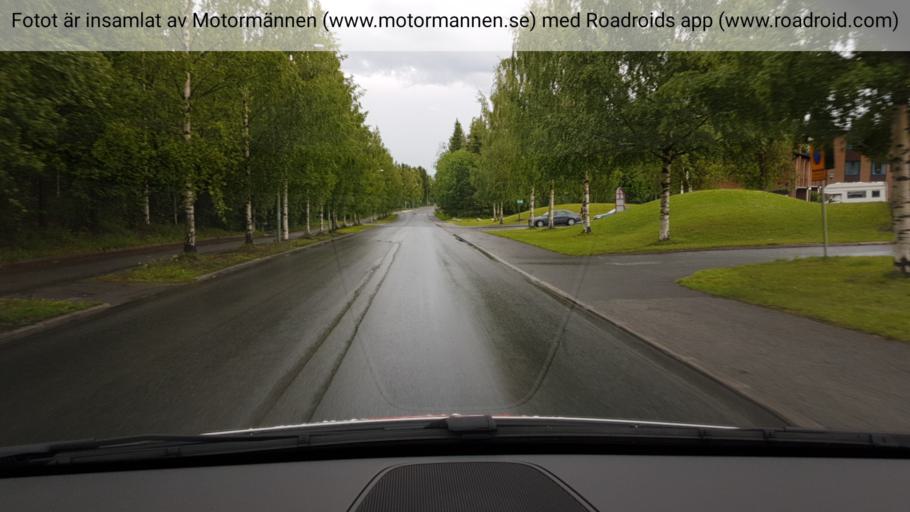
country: SE
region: Jaemtland
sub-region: OEstersunds Kommun
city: Ostersund
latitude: 63.1776
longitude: 14.6822
